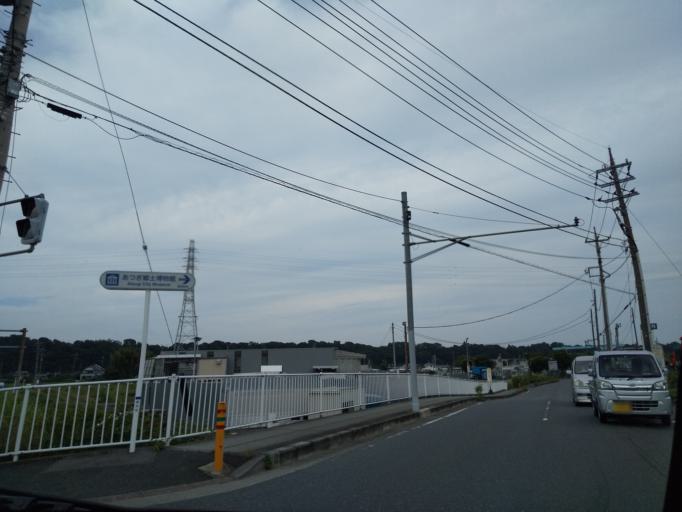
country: JP
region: Kanagawa
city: Zama
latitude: 35.4979
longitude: 139.3461
